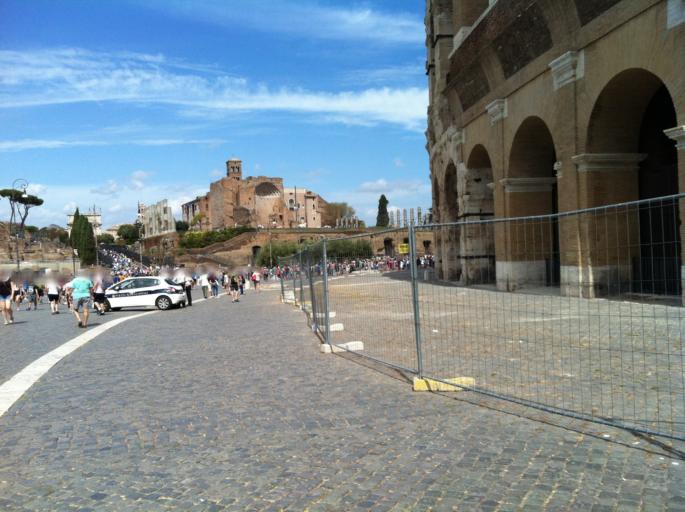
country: IT
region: Latium
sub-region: Citta metropolitana di Roma Capitale
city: Rome
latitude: 41.8896
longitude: 12.4919
